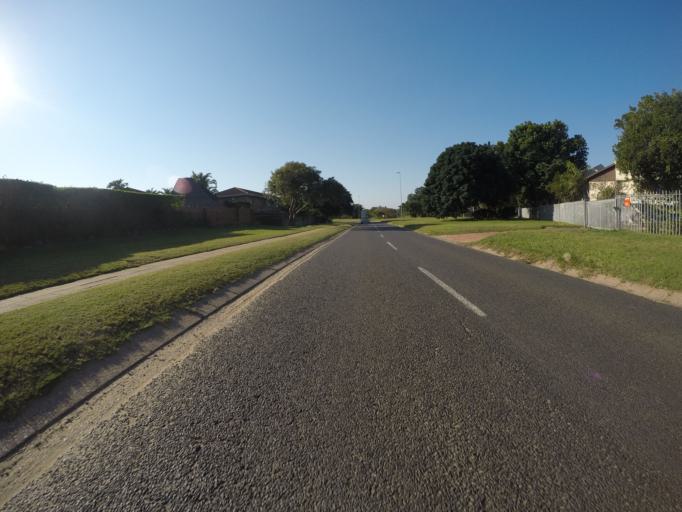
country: ZA
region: KwaZulu-Natal
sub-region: uThungulu District Municipality
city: Richards Bay
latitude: -28.7924
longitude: 32.0977
